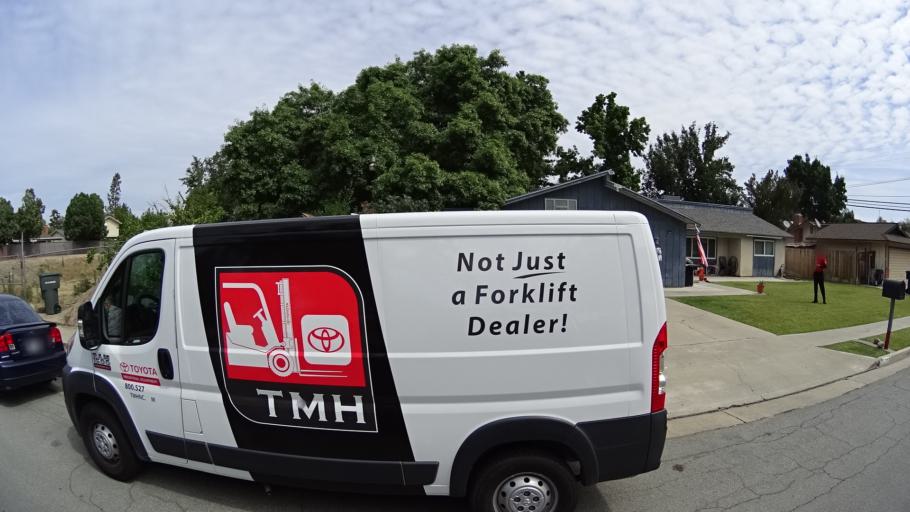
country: US
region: California
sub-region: Kings County
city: Hanford
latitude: 36.3517
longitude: -119.6558
